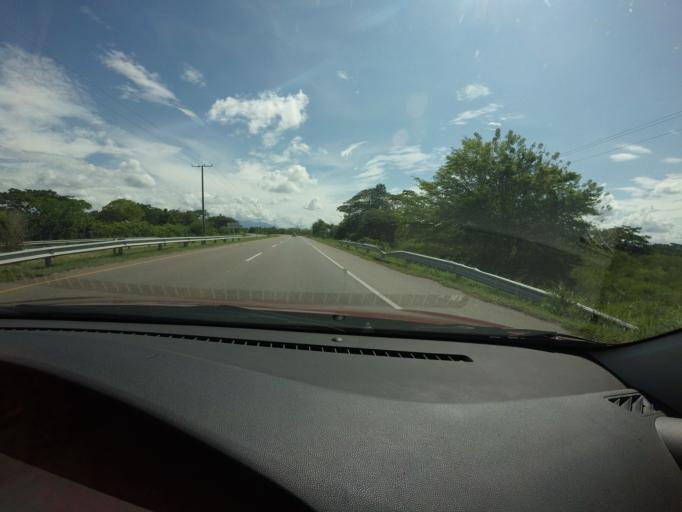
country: CO
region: Antioquia
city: Puerto Triunfo
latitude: 5.7185
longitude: -74.6224
